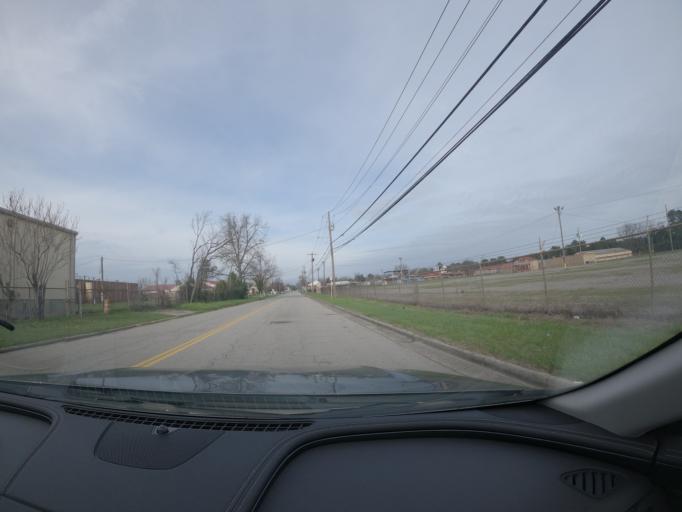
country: US
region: Georgia
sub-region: Richmond County
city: Augusta
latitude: 33.4605
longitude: -81.9620
